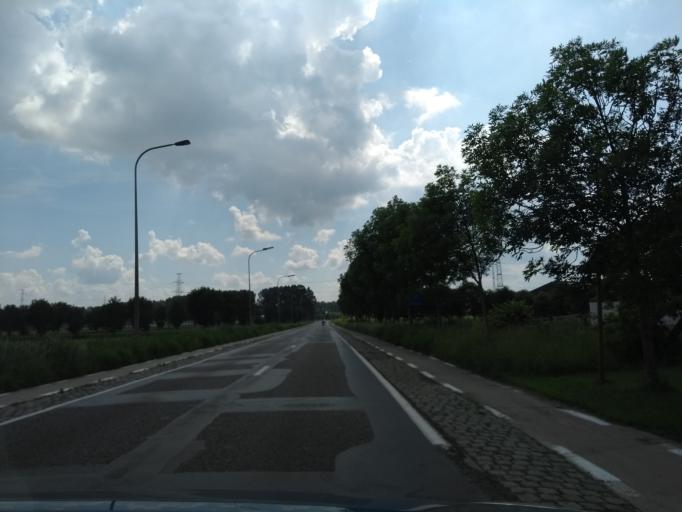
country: BE
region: Flanders
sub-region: Provincie Oost-Vlaanderen
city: Eeklo
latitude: 51.1757
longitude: 3.5470
